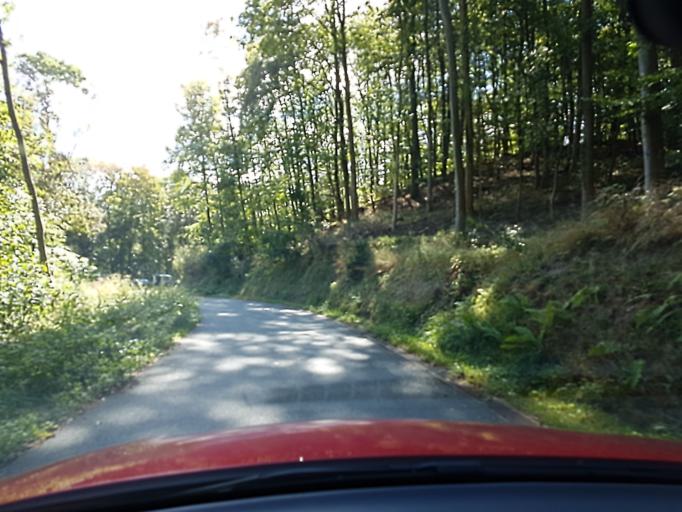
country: DE
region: Hesse
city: Zwingenberg
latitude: 49.7105
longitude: 8.6376
